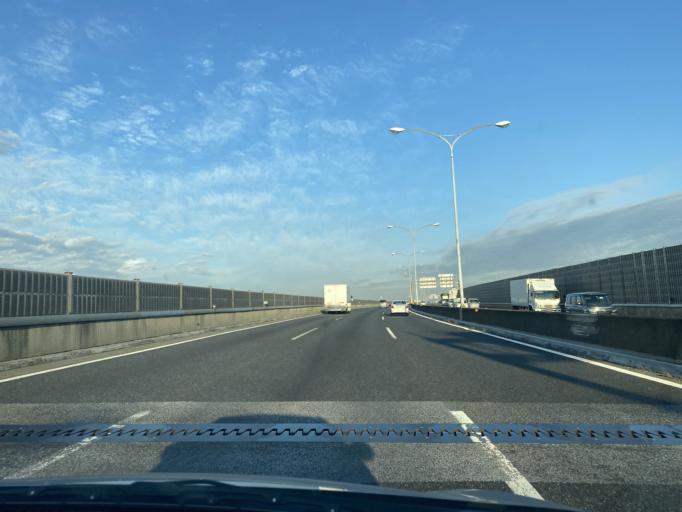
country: JP
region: Osaka
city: Takaishi
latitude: 34.5222
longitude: 135.4952
